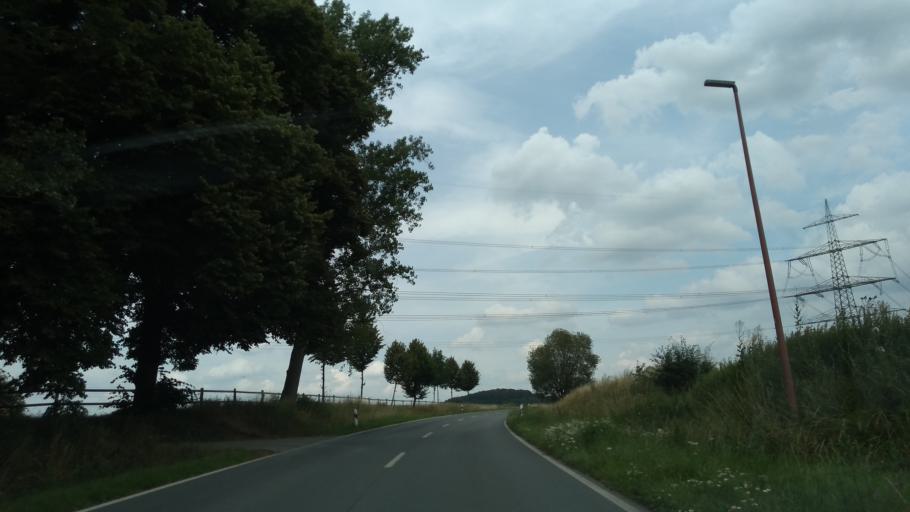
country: DE
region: North Rhine-Westphalia
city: Schwerte
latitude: 51.4596
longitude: 7.6031
